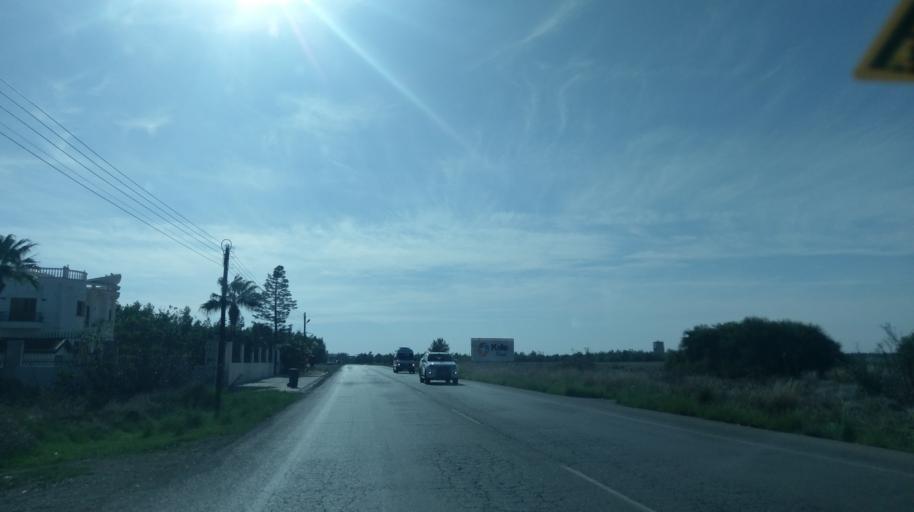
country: CY
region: Ammochostos
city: Trikomo
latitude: 35.2978
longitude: 33.9363
